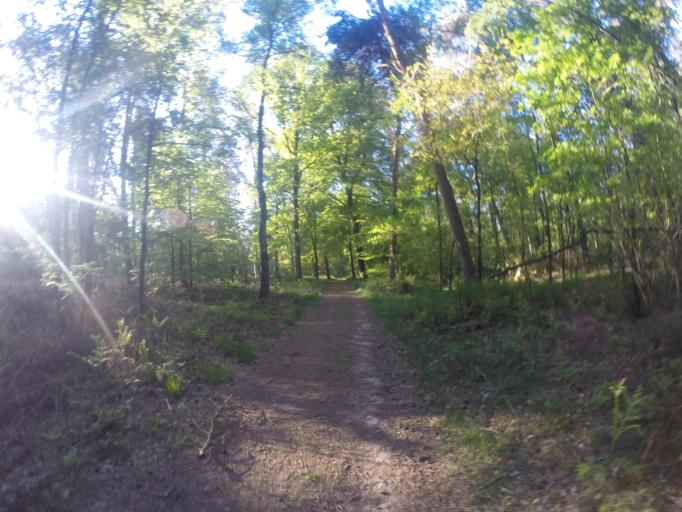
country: NL
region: Gelderland
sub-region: Gemeente Montferland
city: s-Heerenberg
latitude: 51.9011
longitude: 6.2146
